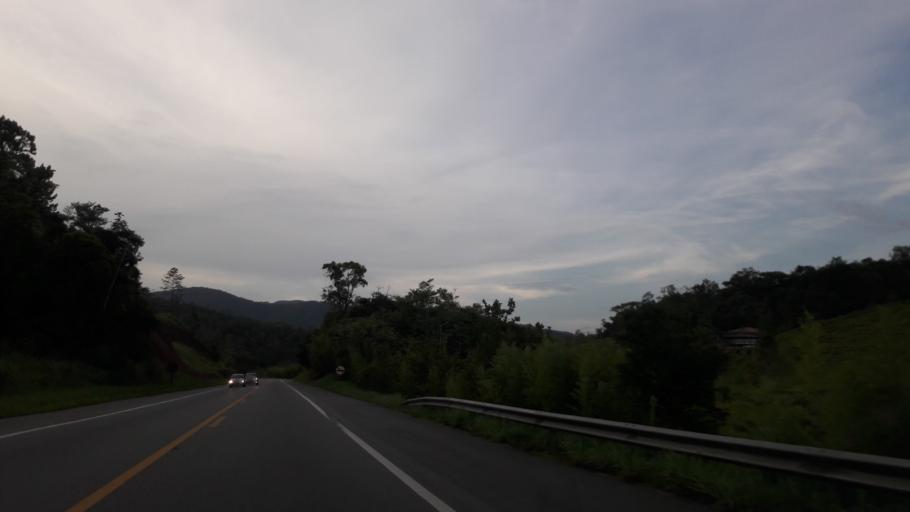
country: BR
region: Sao Paulo
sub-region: Miracatu
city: Miracatu
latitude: -24.2709
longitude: -47.2631
